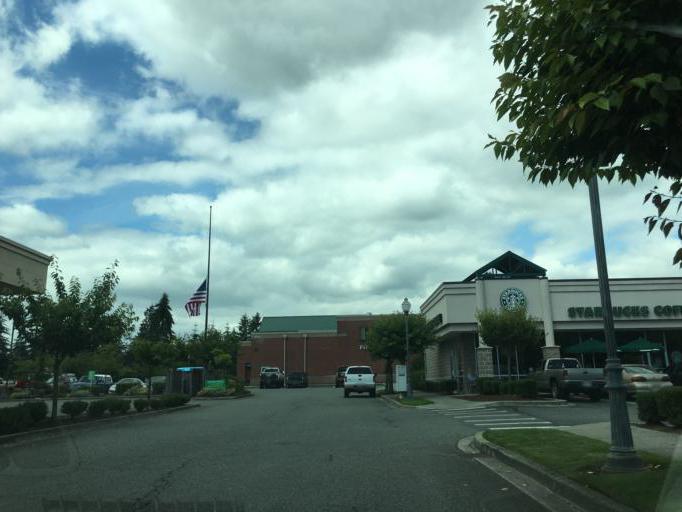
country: US
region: Washington
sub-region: Snohomish County
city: Marysville
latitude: 48.0759
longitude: -122.1809
